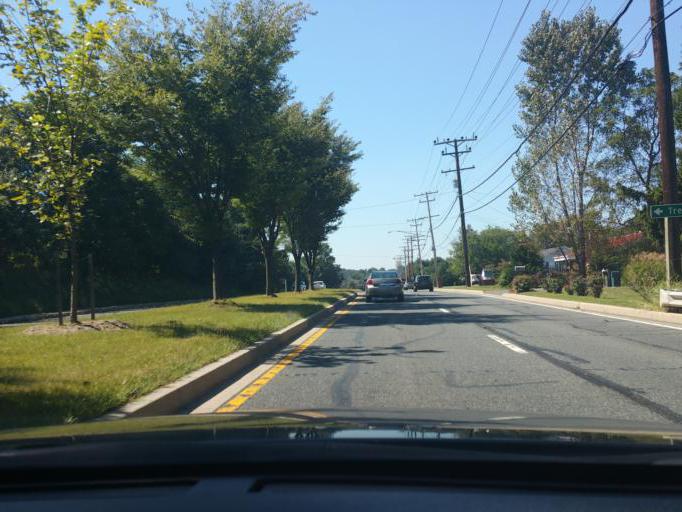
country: US
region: Maryland
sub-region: Harford County
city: South Bel Air
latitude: 39.5460
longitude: -76.3179
